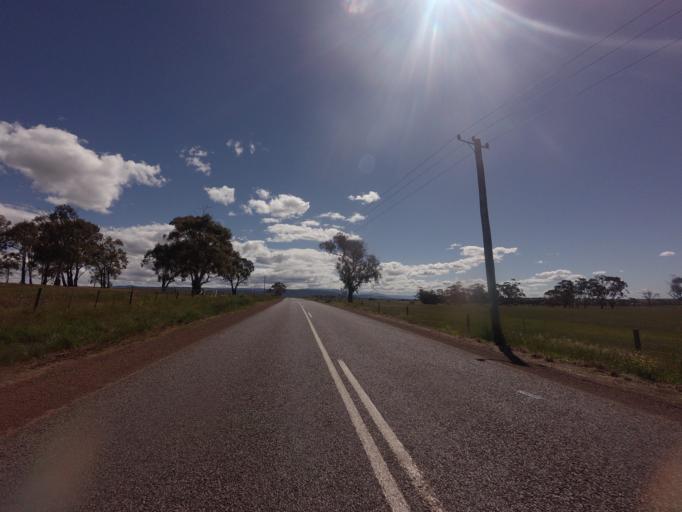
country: AU
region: Tasmania
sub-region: Northern Midlands
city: Evandale
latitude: -41.9430
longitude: 147.5324
